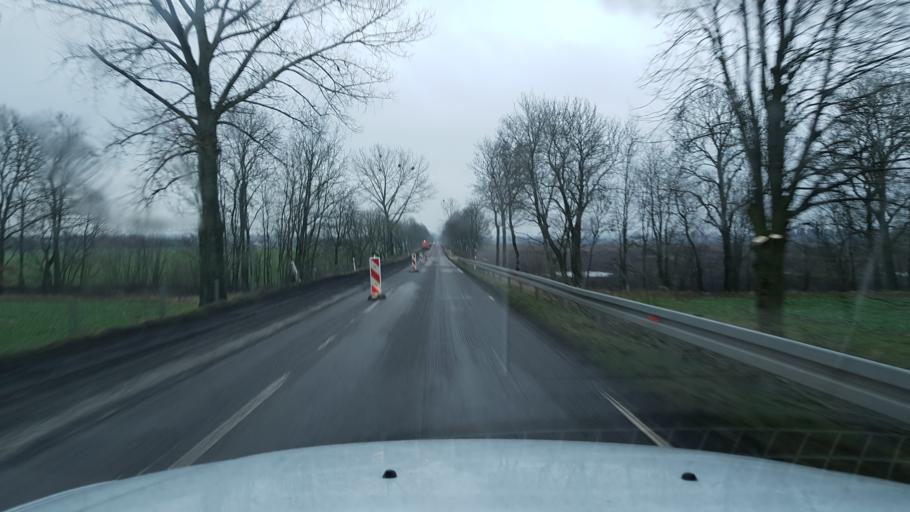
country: PL
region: West Pomeranian Voivodeship
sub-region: Powiat gryficki
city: Ploty
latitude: 53.8303
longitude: 15.2449
